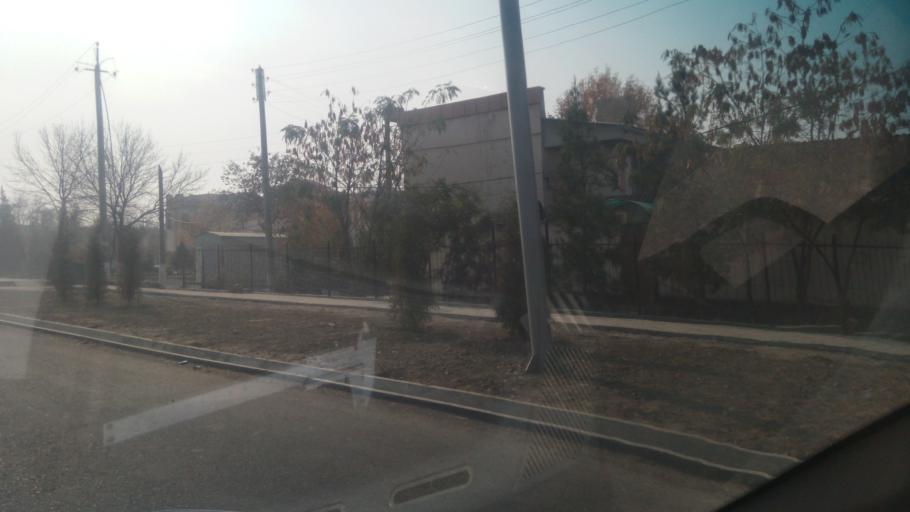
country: UZ
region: Sirdaryo
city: Guliston
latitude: 40.5081
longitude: 68.7734
